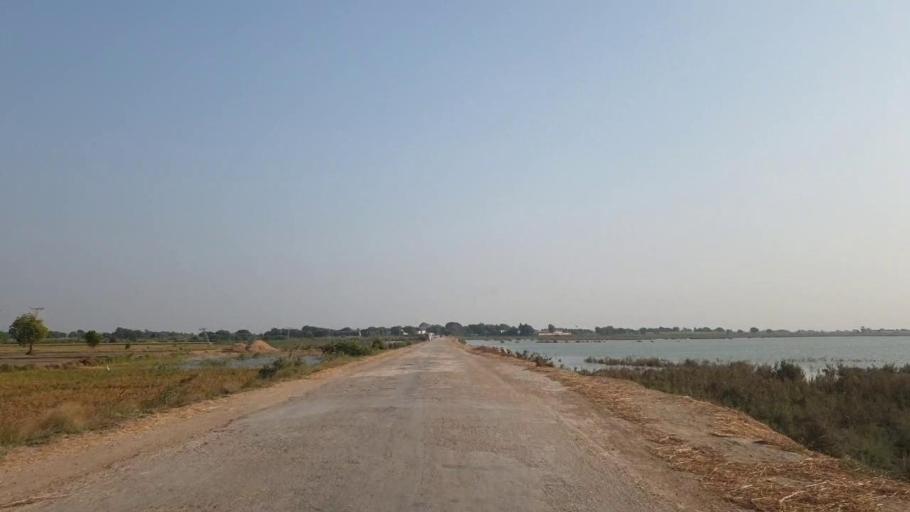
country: PK
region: Sindh
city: Bulri
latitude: 24.9911
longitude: 68.3870
